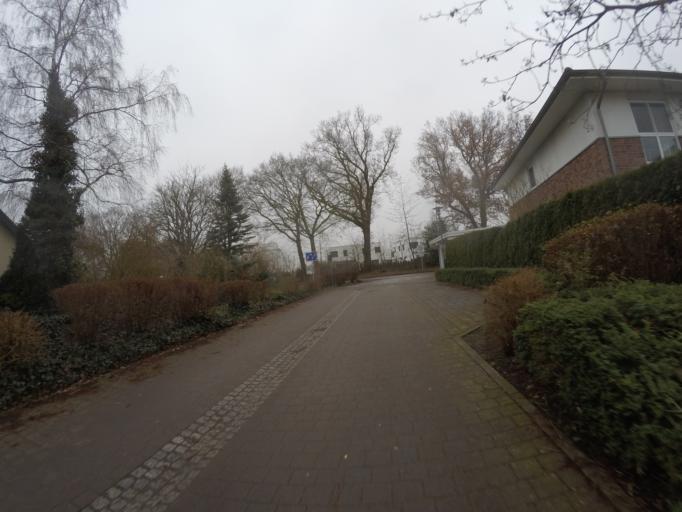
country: DE
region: Schleswig-Holstein
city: Quickborn
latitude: 53.7336
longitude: 9.8879
